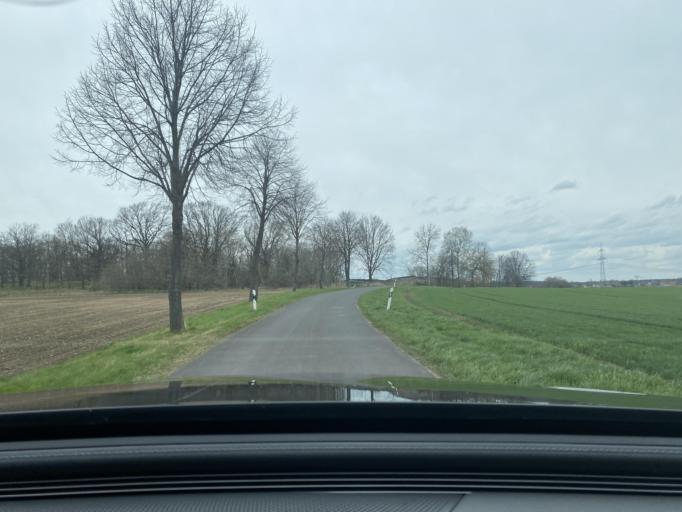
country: DE
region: Saxony
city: Neschwitz
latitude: 51.2318
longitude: 14.3412
